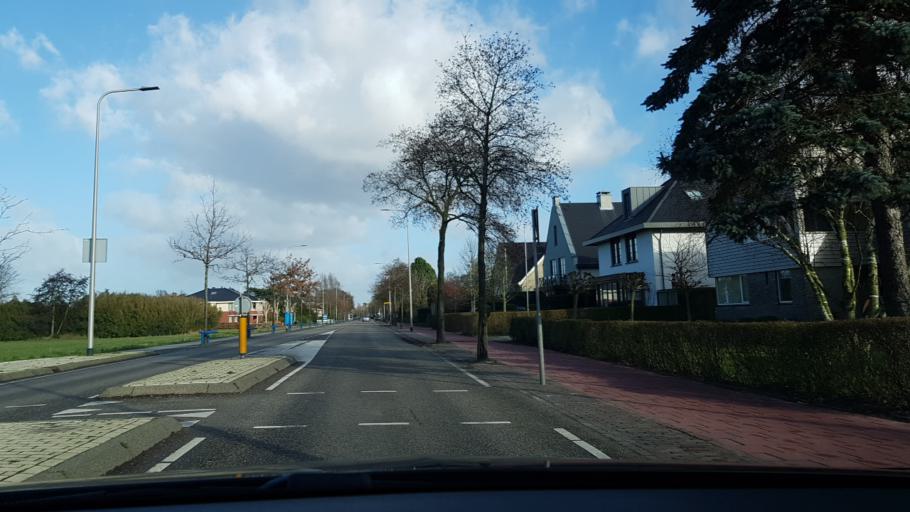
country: NL
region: South Holland
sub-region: Gemeente Teylingen
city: Sassenheim
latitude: 52.2162
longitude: 4.5046
